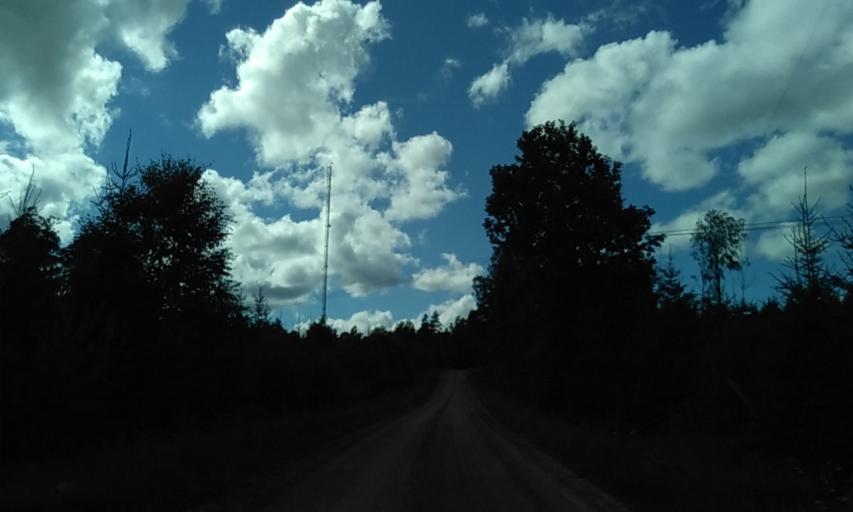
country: SE
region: Vaestra Goetaland
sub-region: Vargarda Kommun
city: Vargarda
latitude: 58.0023
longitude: 12.9002
